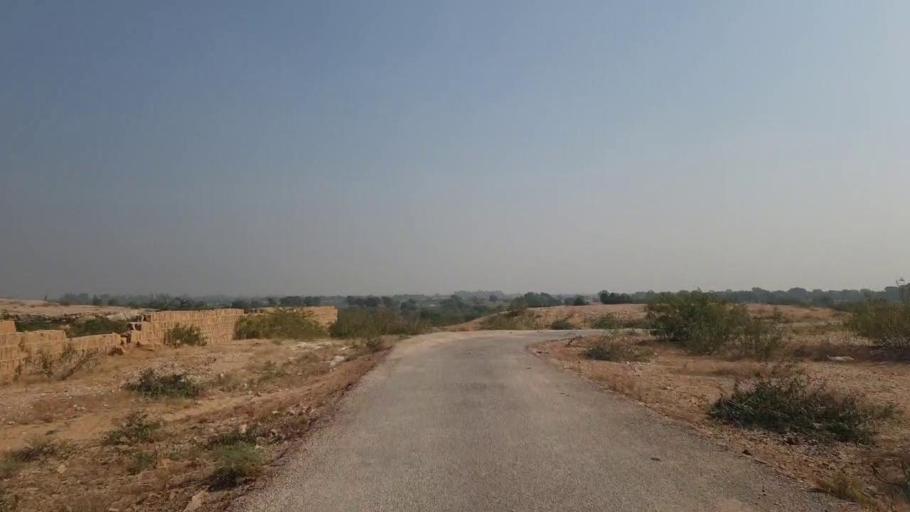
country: PK
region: Sindh
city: Kotri
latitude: 25.3196
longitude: 68.2683
